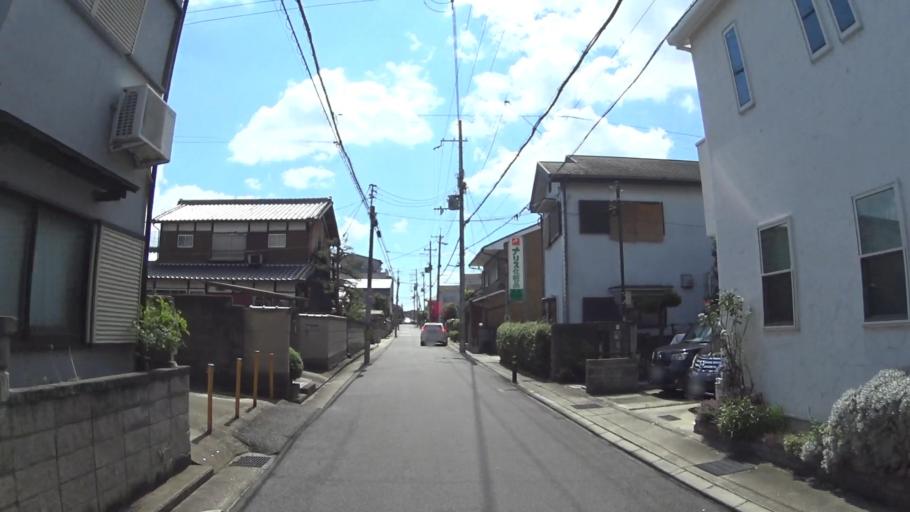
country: JP
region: Kyoto
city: Uji
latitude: 34.8787
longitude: 135.7790
